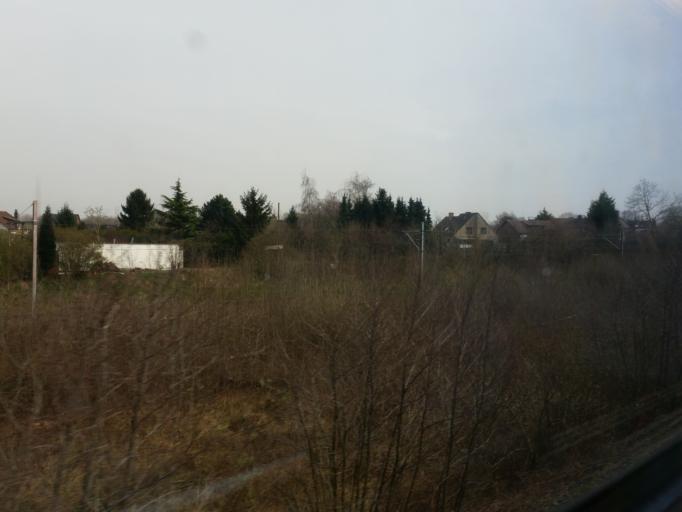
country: BE
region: Flanders
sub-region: Provincie Vlaams-Brabant
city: Liedekerke
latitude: 50.8807
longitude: 4.1148
